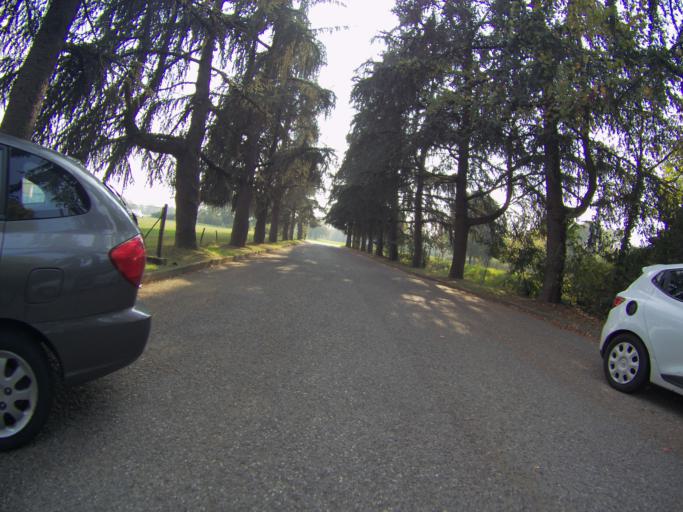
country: IT
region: Emilia-Romagna
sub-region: Provincia di Reggio Emilia
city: Forche
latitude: 44.6619
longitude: 10.5840
